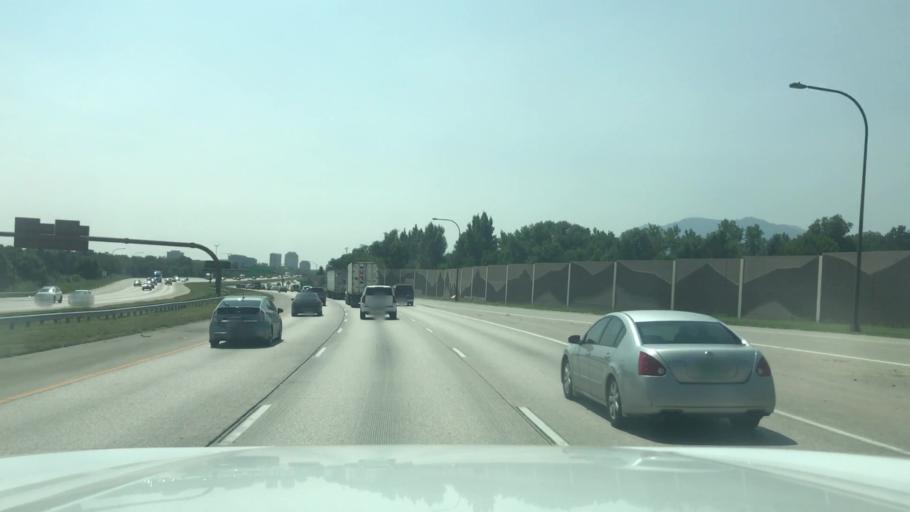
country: US
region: Colorado
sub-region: El Paso County
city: Colorado Springs
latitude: 38.8583
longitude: -104.8344
